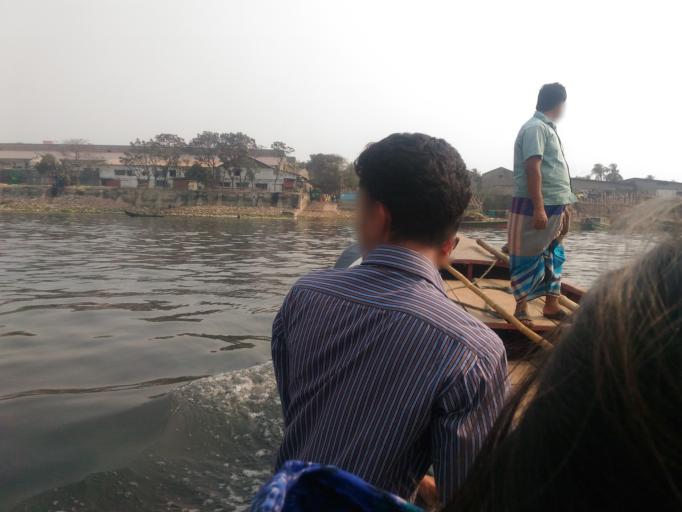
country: BD
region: Dhaka
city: Narayanganj
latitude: 23.6322
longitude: 90.4601
